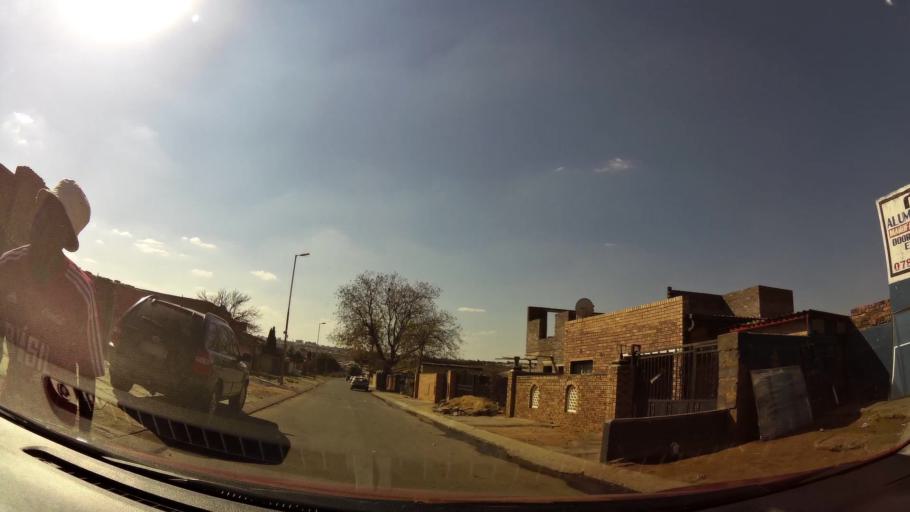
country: ZA
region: Gauteng
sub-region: City of Johannesburg Metropolitan Municipality
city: Soweto
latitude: -26.2338
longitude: 27.8830
